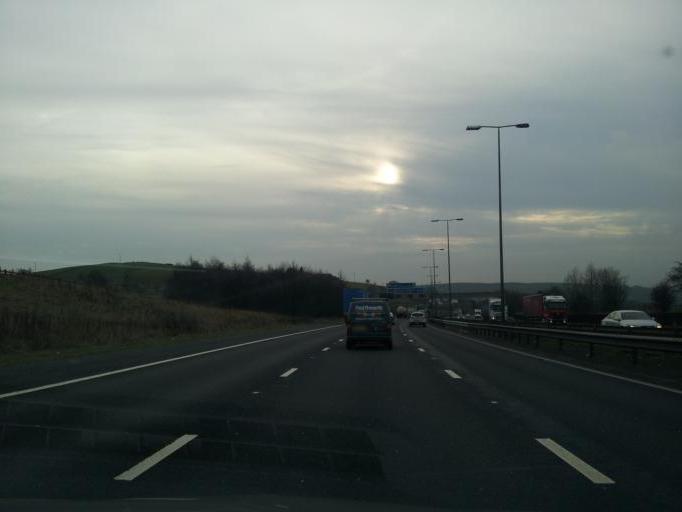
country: GB
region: England
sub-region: Borough of Rochdale
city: Milnrow
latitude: 53.6139
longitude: -2.0891
